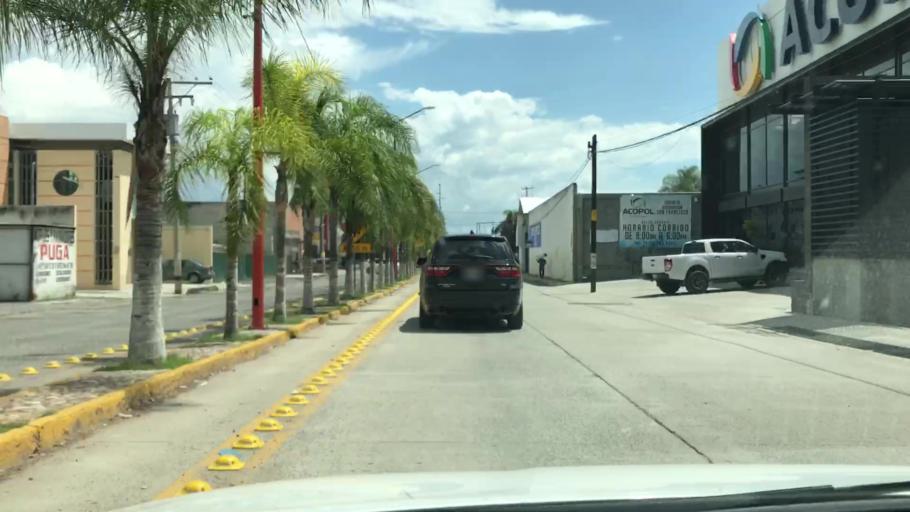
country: MX
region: Guanajuato
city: San Francisco del Rincon
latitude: 21.0309
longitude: -101.8531
